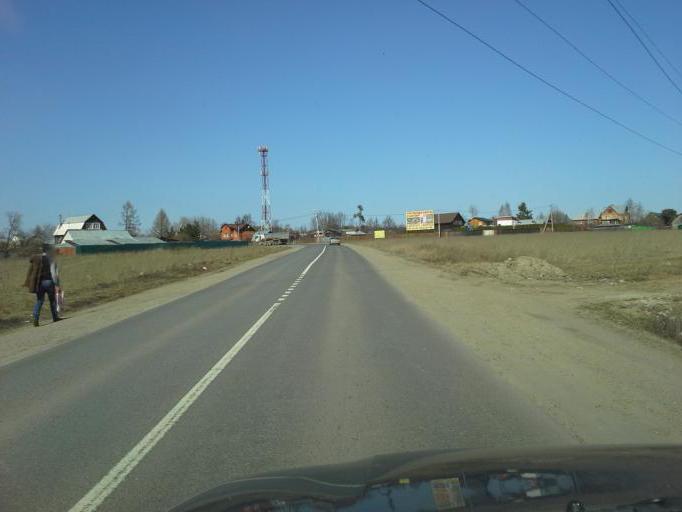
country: RU
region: Moskovskaya
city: Kokoshkino
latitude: 55.6113
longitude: 37.1650
